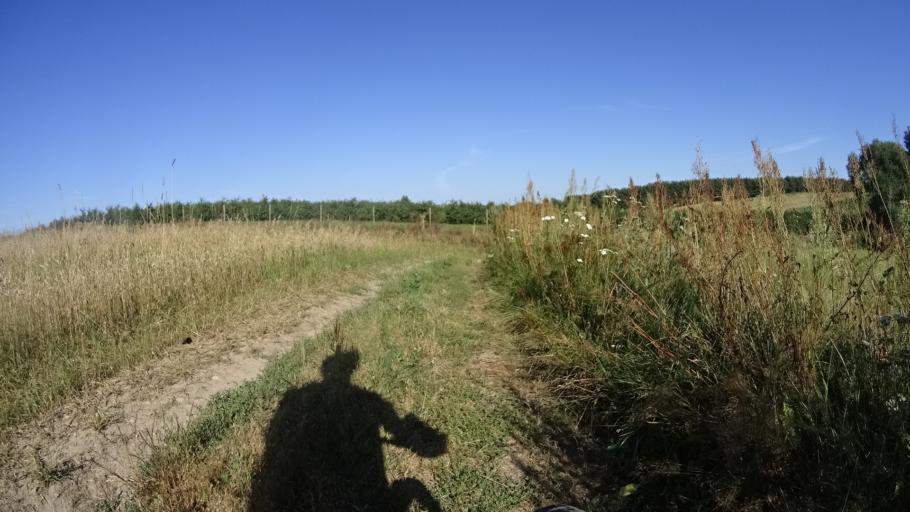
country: PL
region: Masovian Voivodeship
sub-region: Powiat bialobrzeski
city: Wysmierzyce
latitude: 51.6720
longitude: 20.8484
